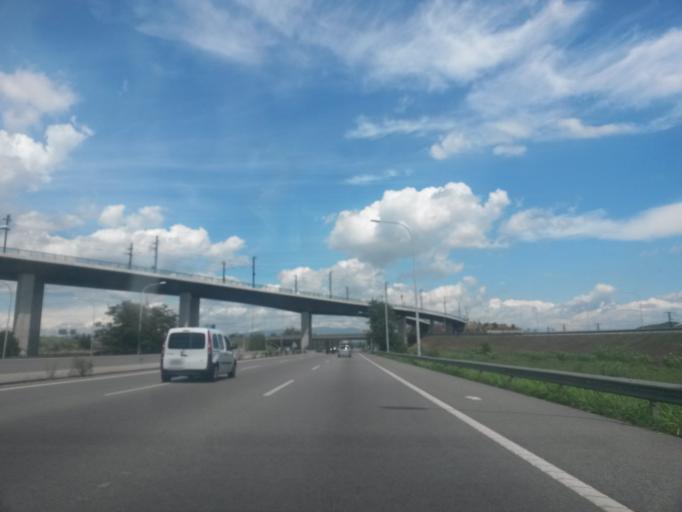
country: ES
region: Catalonia
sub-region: Provincia de Barcelona
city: Mollet del Valles
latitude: 41.5217
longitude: 2.2124
